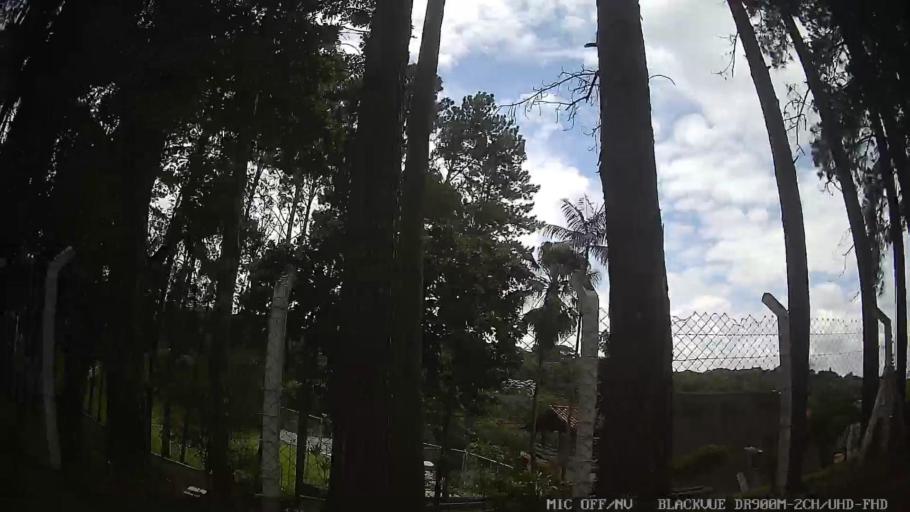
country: BR
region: Sao Paulo
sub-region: Aruja
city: Aruja
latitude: -23.4169
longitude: -46.3404
